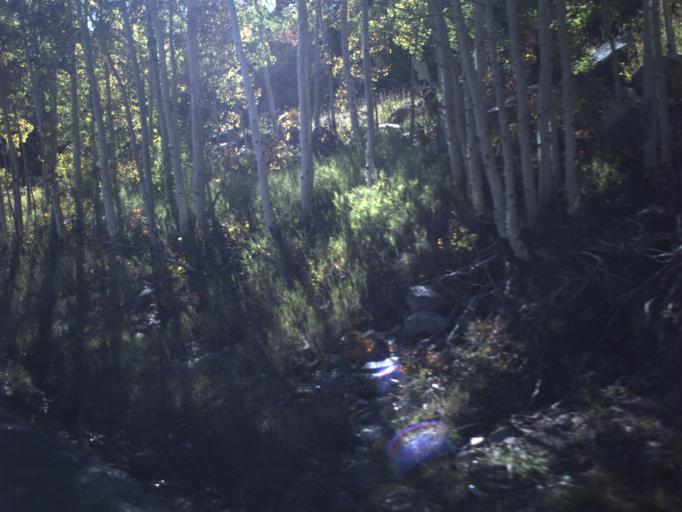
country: US
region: Utah
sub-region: Iron County
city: Parowan
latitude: 37.6967
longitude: -112.8460
